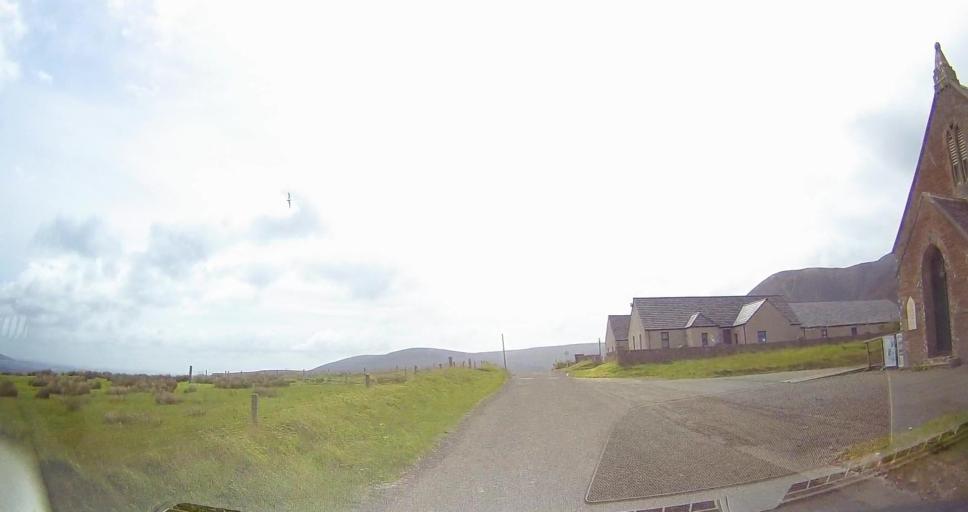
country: GB
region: Scotland
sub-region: Orkney Islands
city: Stromness
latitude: 58.9139
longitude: -3.3329
